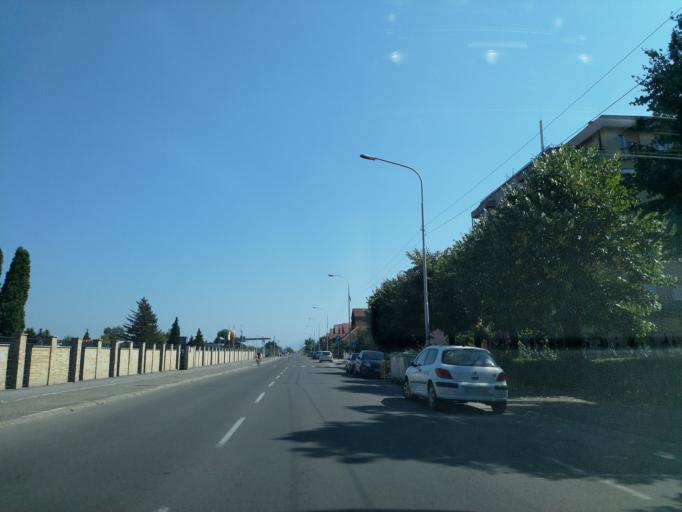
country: RS
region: Central Serbia
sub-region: Rasinski Okrug
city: Trstenik
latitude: 43.6165
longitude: 21.0101
